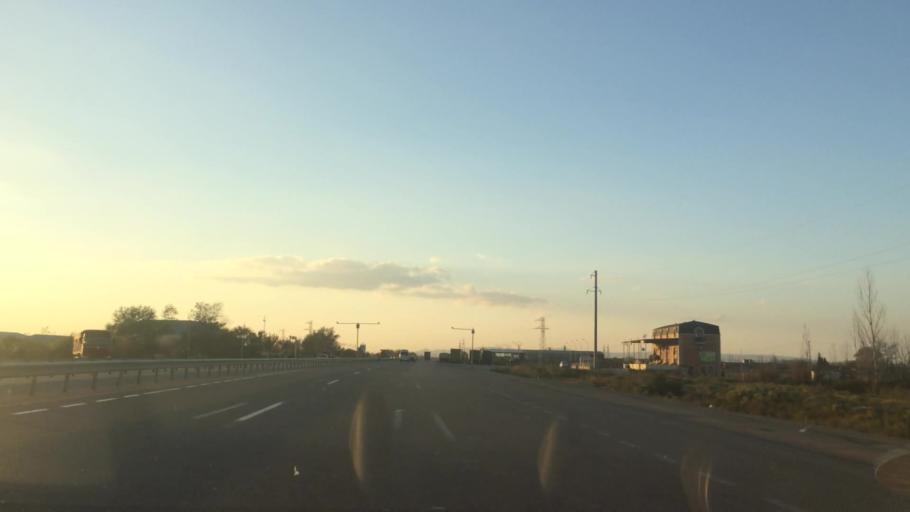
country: AZ
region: Haciqabul
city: Haciqabul
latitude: 40.0089
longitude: 49.1540
